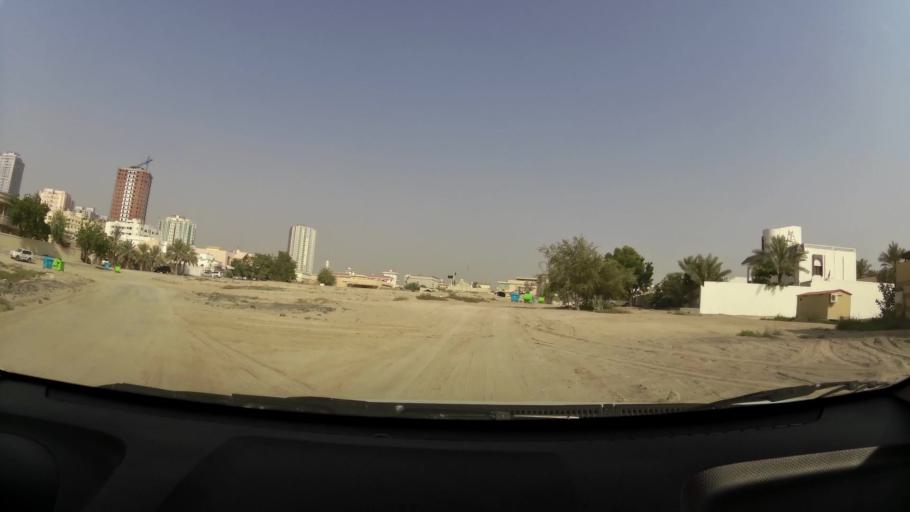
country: AE
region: Ajman
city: Ajman
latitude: 25.3893
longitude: 55.4320
